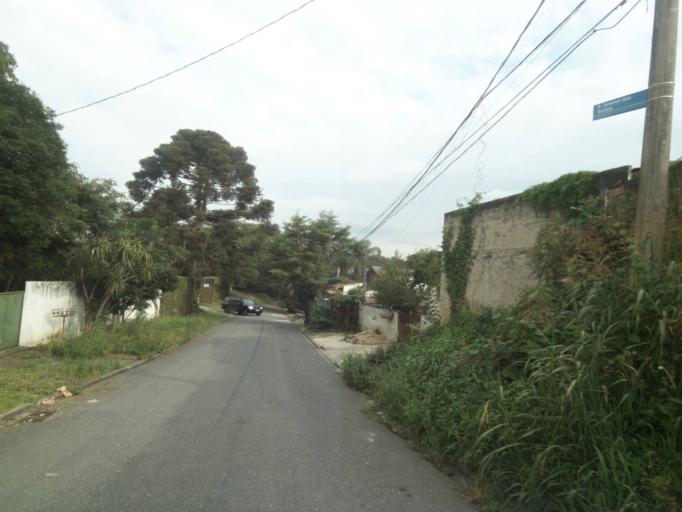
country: BR
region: Parana
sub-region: Curitiba
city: Curitiba
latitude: -25.4087
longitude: -49.3081
